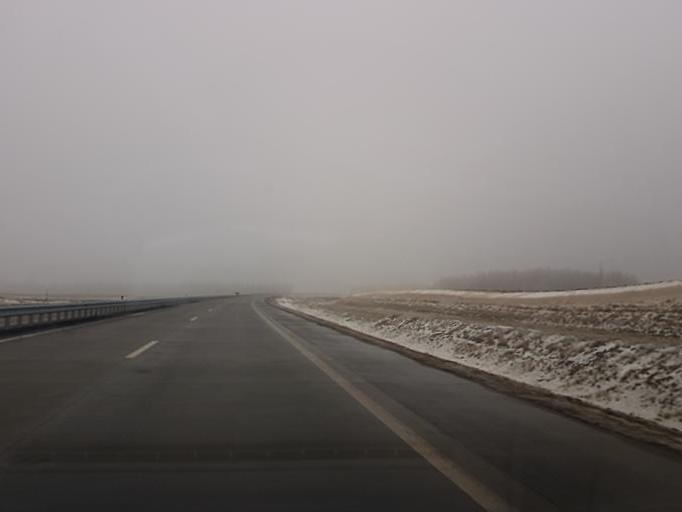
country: BY
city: Fanipol
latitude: 53.7633
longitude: 27.3808
